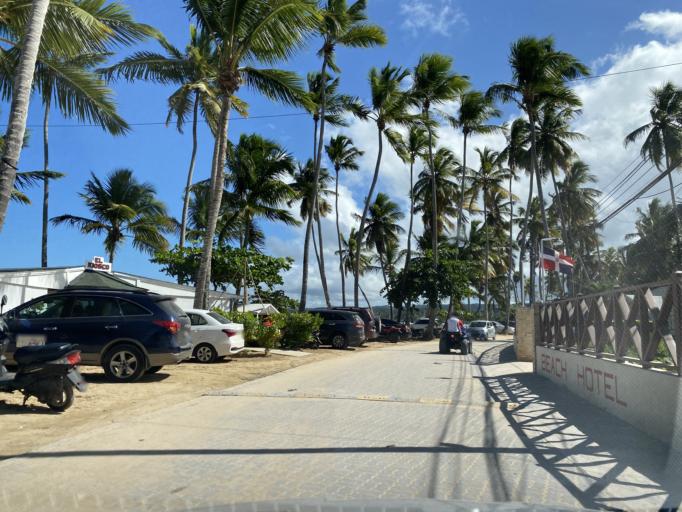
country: DO
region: Samana
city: Las Terrenas
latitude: 19.3265
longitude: -69.5450
